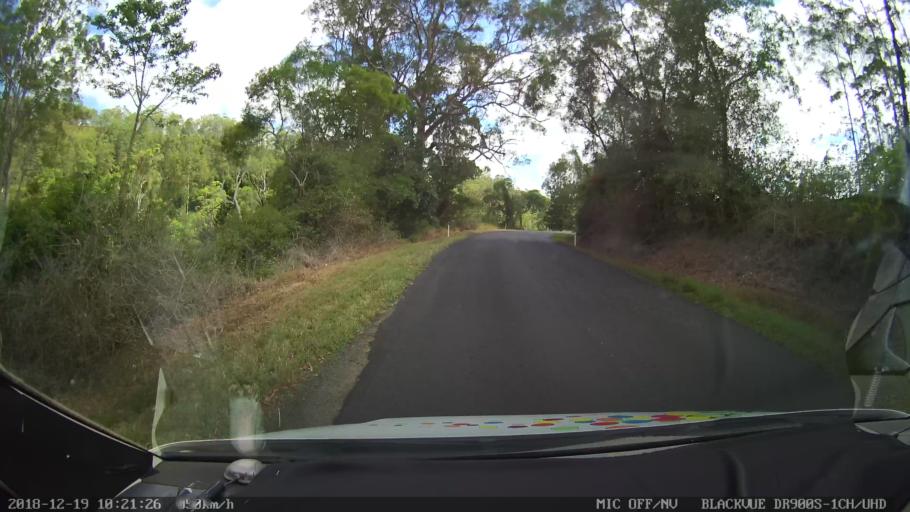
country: AU
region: New South Wales
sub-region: Kyogle
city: Kyogle
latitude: -28.5981
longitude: 153.0598
